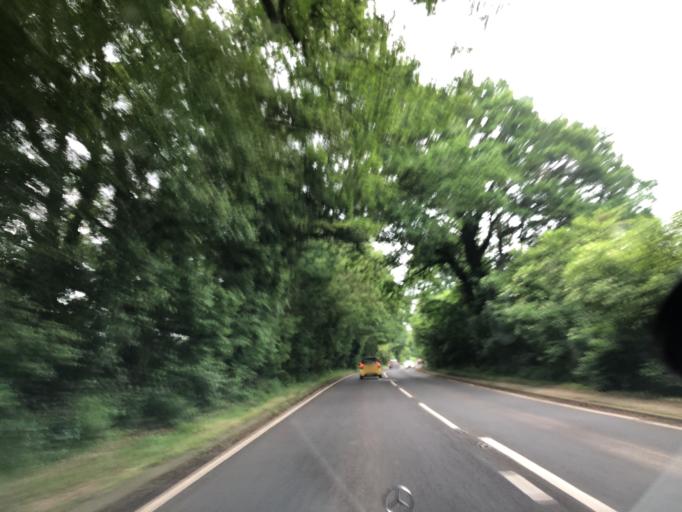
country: GB
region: England
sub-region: Warwickshire
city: Wroxall
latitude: 52.3192
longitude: -1.6671
